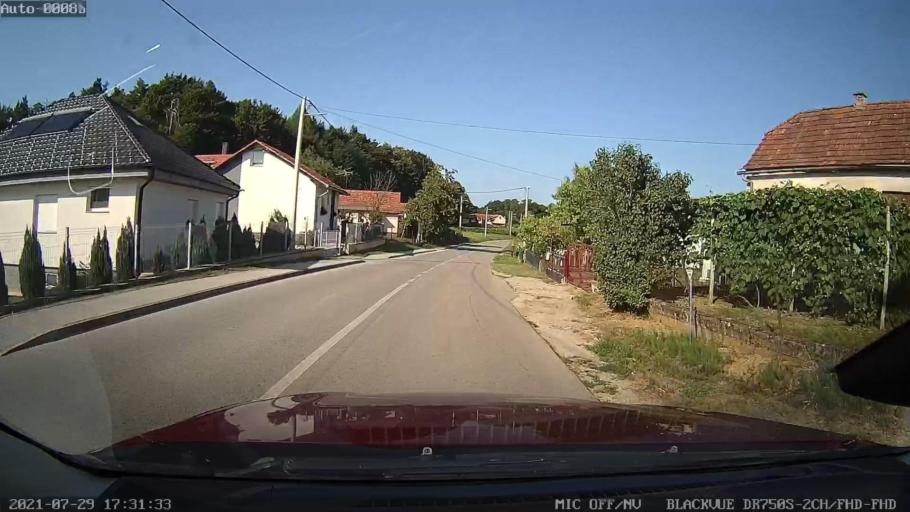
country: HR
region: Varazdinska
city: Vinica
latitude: 46.2874
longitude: 16.1230
